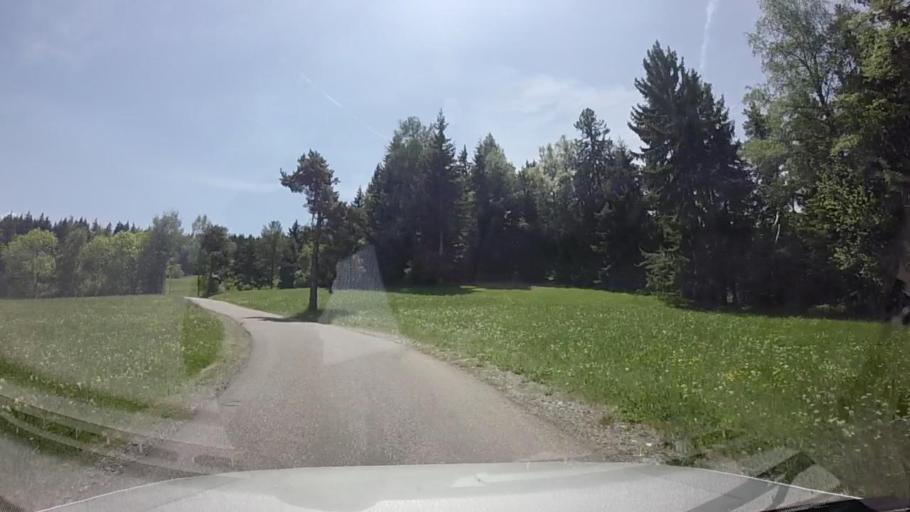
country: FR
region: Provence-Alpes-Cote d'Azur
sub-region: Departement des Alpes-de-Haute-Provence
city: Seyne-les-Alpes
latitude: 44.3318
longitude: 6.3315
